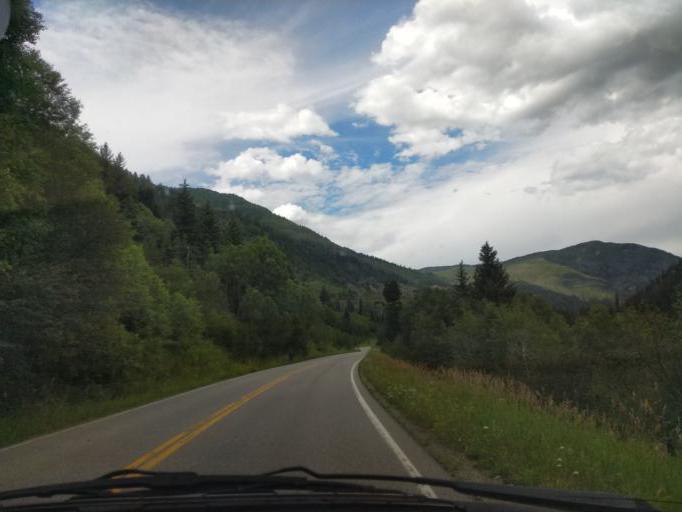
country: US
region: Colorado
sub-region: Garfield County
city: Carbondale
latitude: 39.0999
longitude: -107.2627
